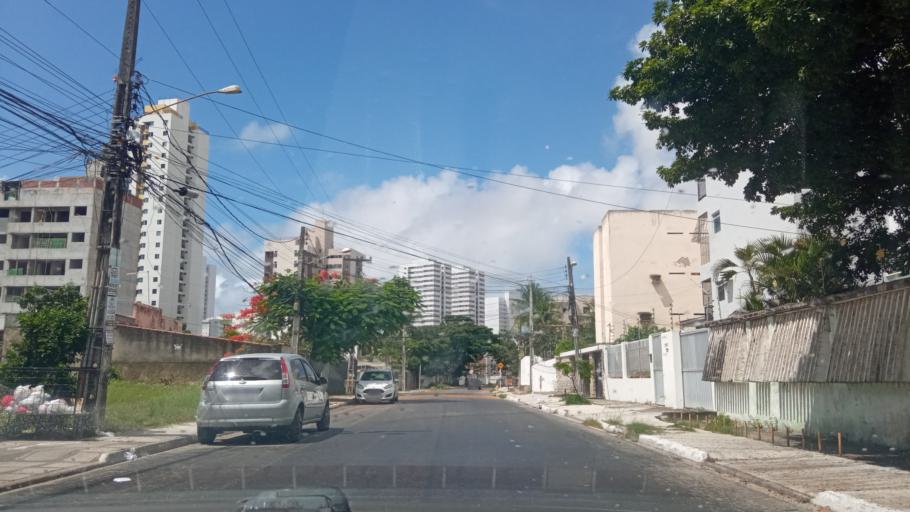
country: BR
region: Pernambuco
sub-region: Jaboatao Dos Guararapes
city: Jaboatao
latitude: -8.1999
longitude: -34.9209
